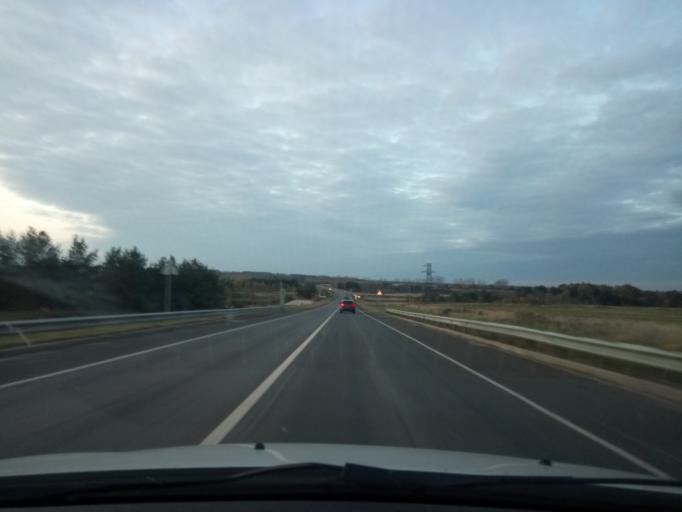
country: RU
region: Nizjnij Novgorod
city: Bol'shoye Murashkino
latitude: 55.8765
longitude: 44.7479
